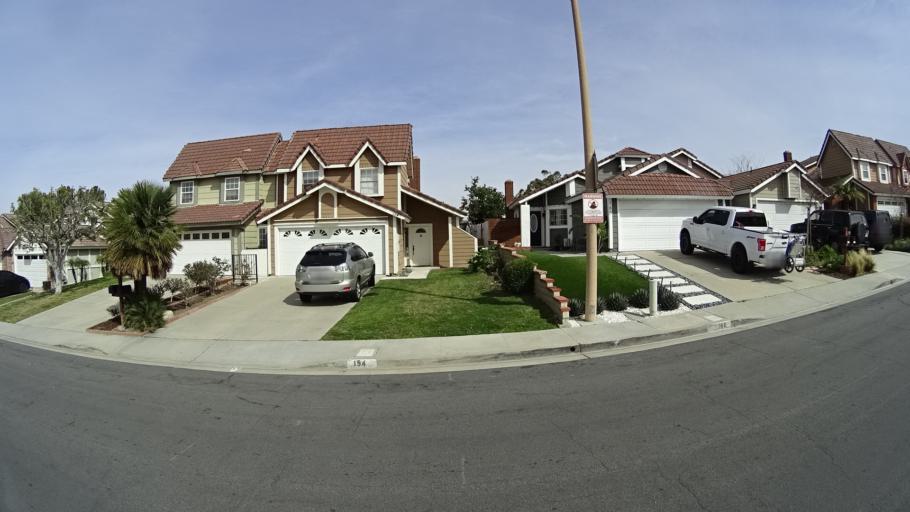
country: US
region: California
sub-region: Orange County
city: Yorba Linda
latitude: 33.8685
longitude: -117.7378
